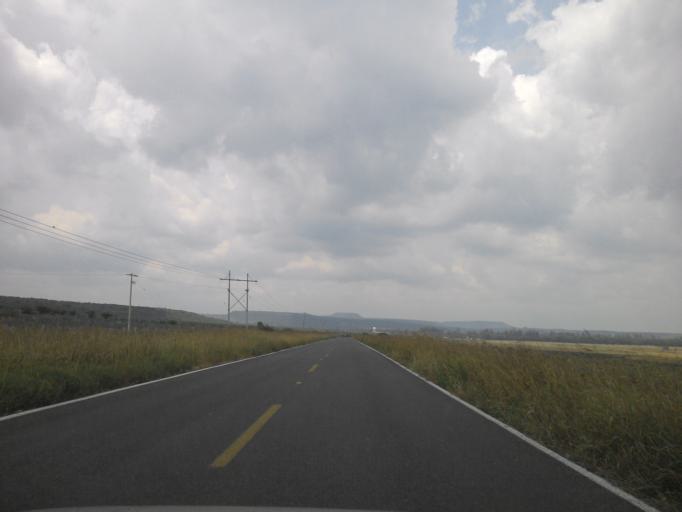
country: MX
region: Jalisco
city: San Diego de Alejandria
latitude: 20.8582
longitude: -101.9970
